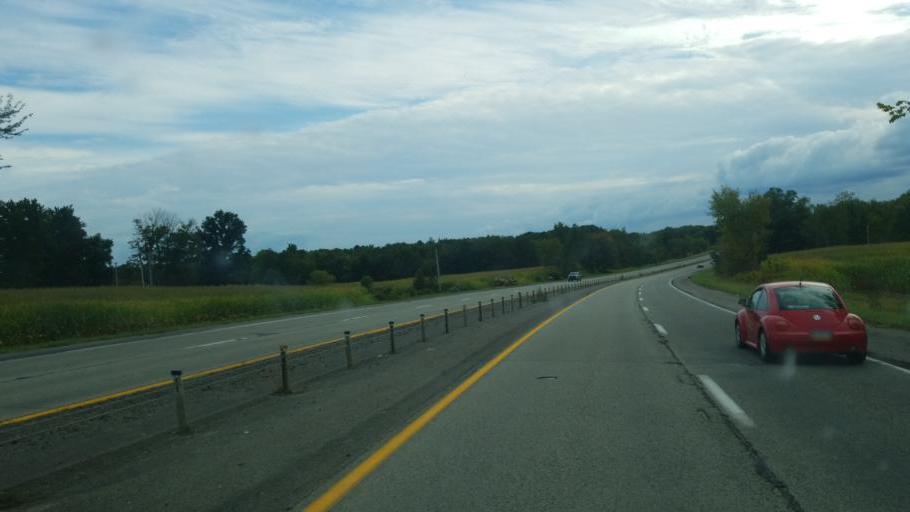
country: US
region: Pennsylvania
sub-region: Mercer County
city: Reynolds Heights
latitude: 41.3095
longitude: -80.4133
